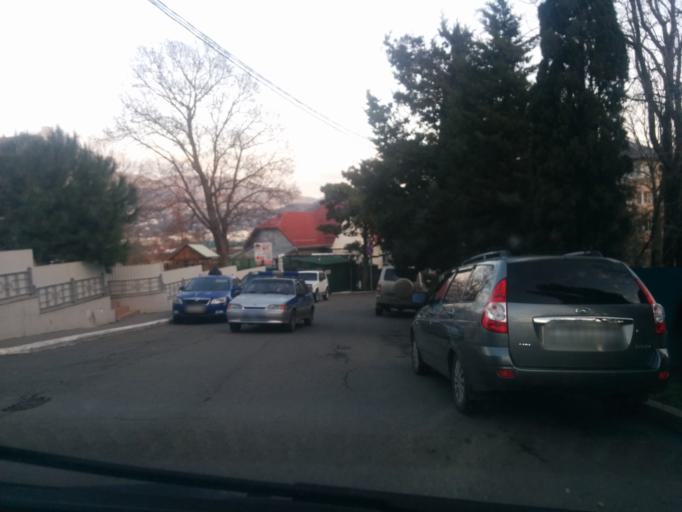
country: RU
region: Krasnodarskiy
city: Tuapse
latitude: 44.1006
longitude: 39.0769
